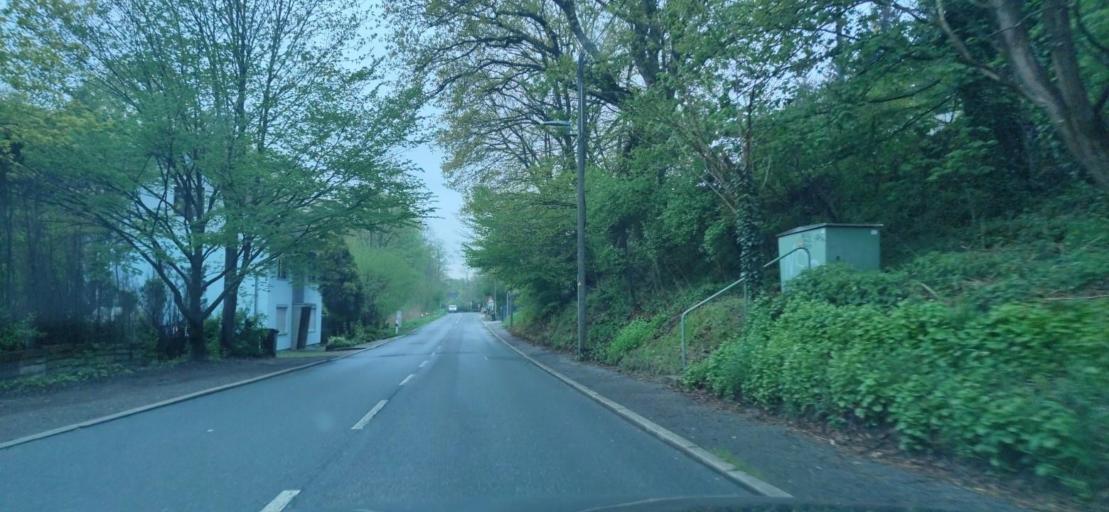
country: DE
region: North Rhine-Westphalia
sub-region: Regierungsbezirk Dusseldorf
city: Velbert
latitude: 51.4081
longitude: 7.0879
